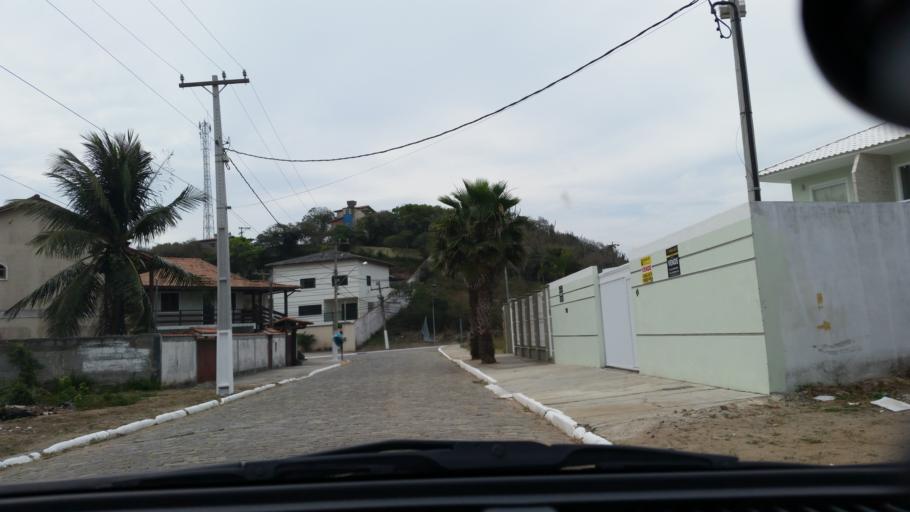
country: BR
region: Rio de Janeiro
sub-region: Cabo Frio
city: Cabo Frio
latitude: -22.8674
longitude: -41.9950
